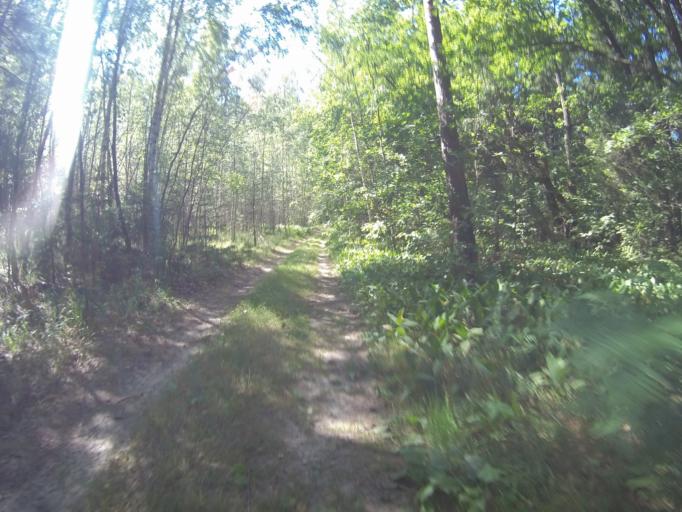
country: RU
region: Vladimir
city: Raduzhnyy
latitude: 56.0217
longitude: 40.2646
